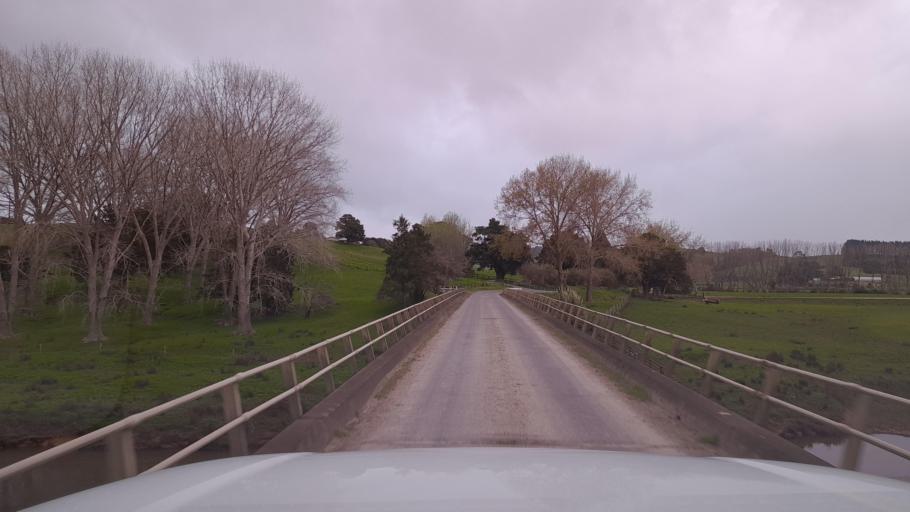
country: NZ
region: Northland
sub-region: Whangarei
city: Maungatapere
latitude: -35.6327
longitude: 174.2001
